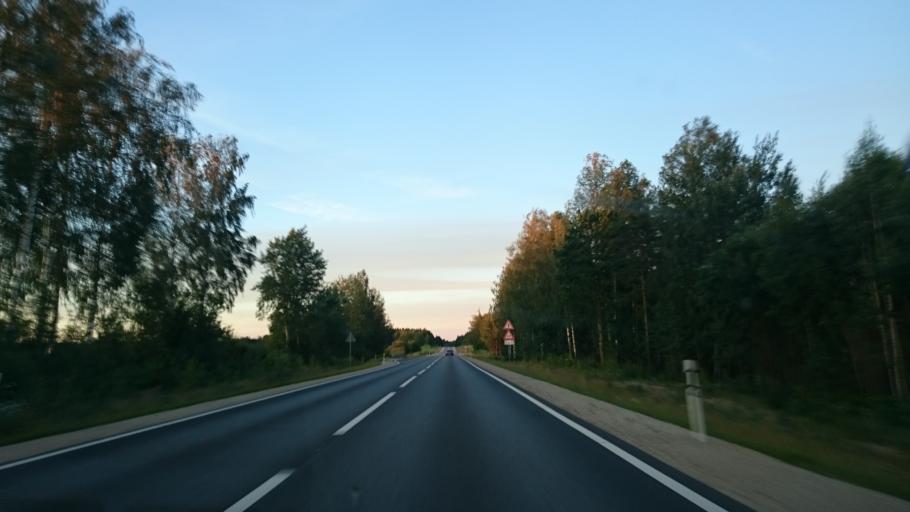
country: LV
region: Jaunpils
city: Jaunpils
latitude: 56.6791
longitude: 23.0930
